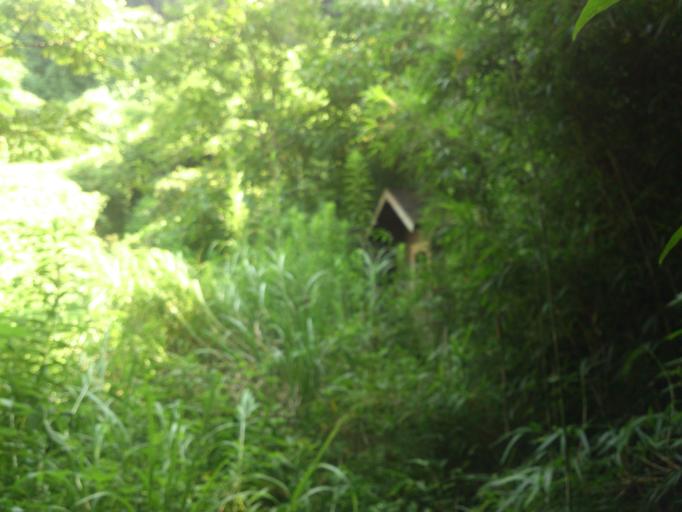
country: JP
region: Chiba
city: Tateyama
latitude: 35.0748
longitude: 139.8342
